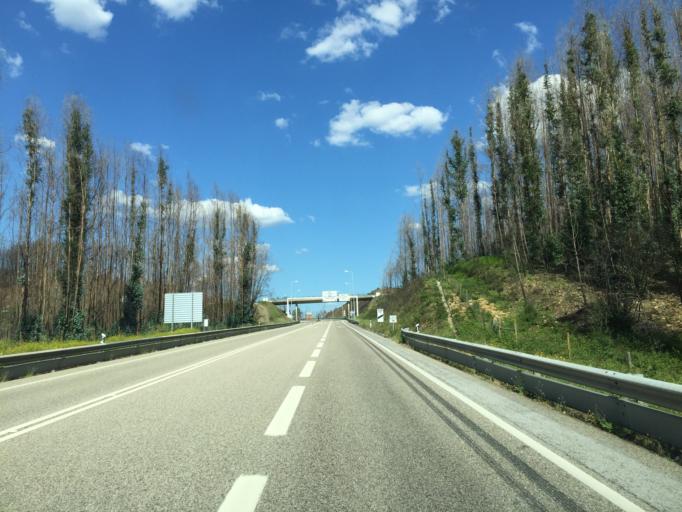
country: PT
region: Leiria
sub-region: Figueiro Dos Vinhos
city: Figueiro dos Vinhos
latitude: 39.9310
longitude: -8.2906
